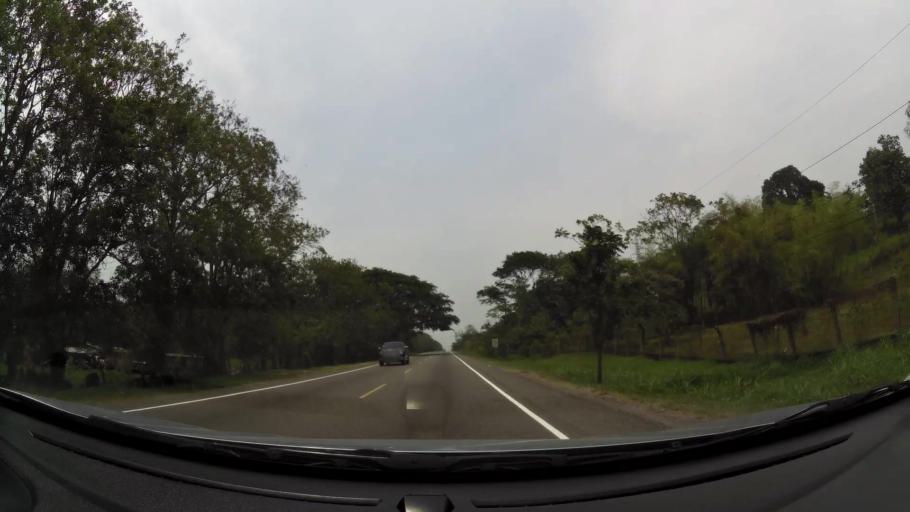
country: HN
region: Cortes
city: La Guama
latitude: 14.8314
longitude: -87.9605
